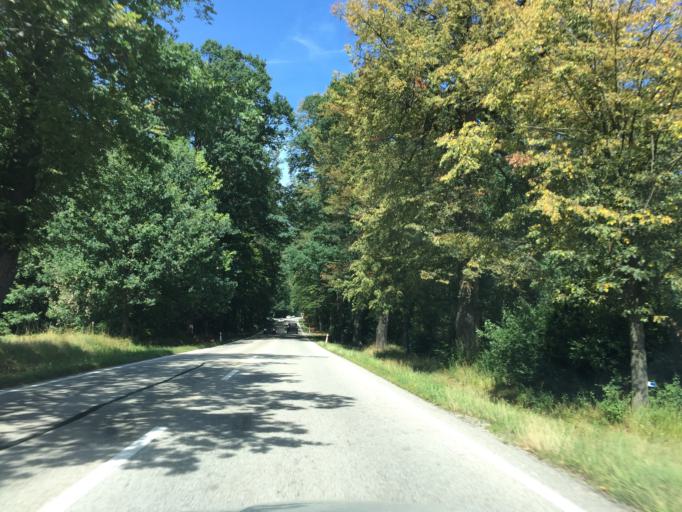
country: CZ
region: Jihocesky
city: Borek
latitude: 49.0478
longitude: 14.5094
